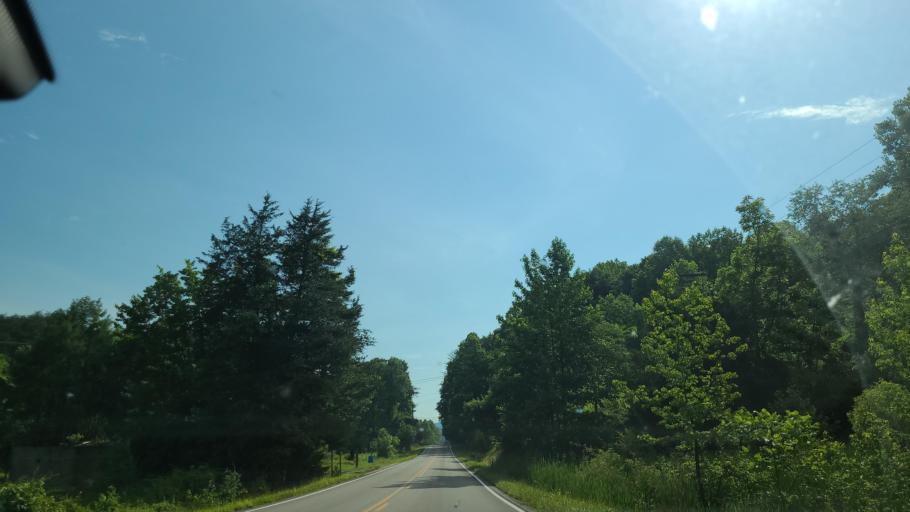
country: US
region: Kentucky
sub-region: Bell County
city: Middlesboro
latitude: 36.6949
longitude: -83.8619
